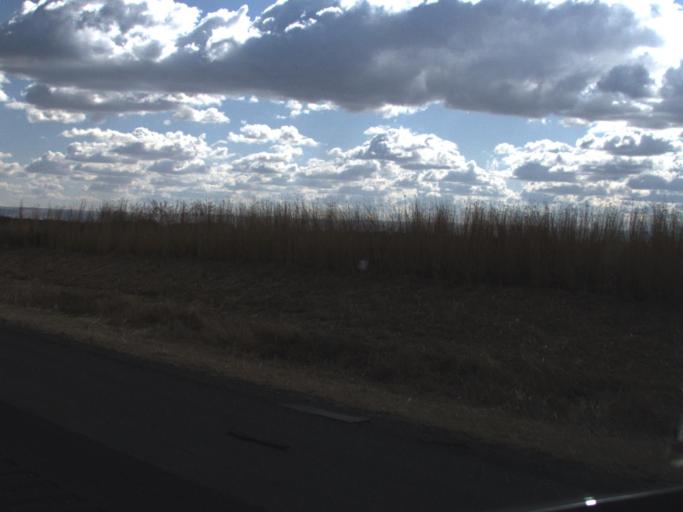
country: US
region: Washington
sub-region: Yakima County
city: Granger
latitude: 46.3586
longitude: -120.2020
